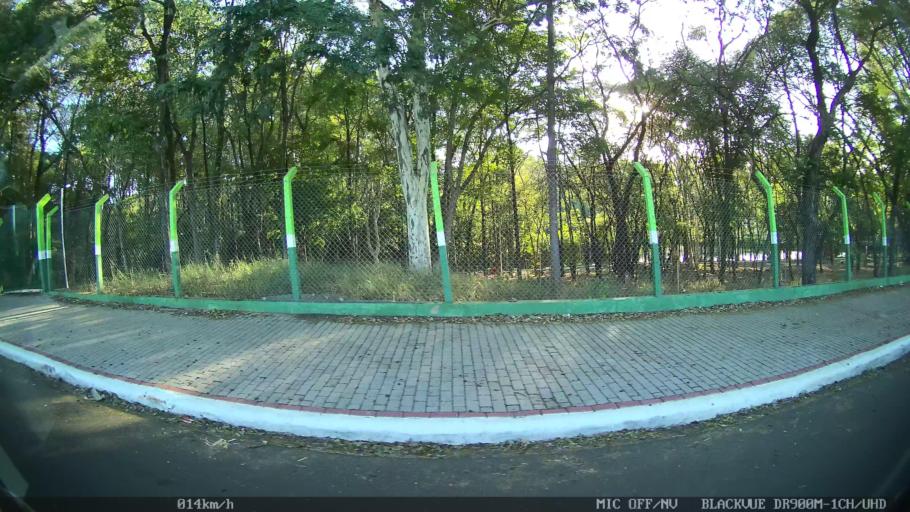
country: BR
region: Sao Paulo
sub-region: Nova Odessa
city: Nova Odessa
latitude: -22.7851
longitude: -47.2929
